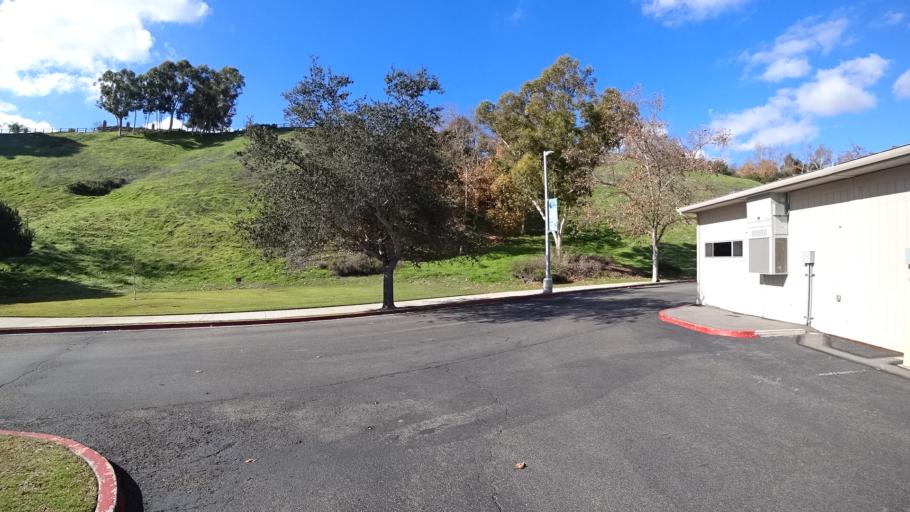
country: US
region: California
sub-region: Orange County
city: Aliso Viejo
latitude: 33.5597
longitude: -117.7201
